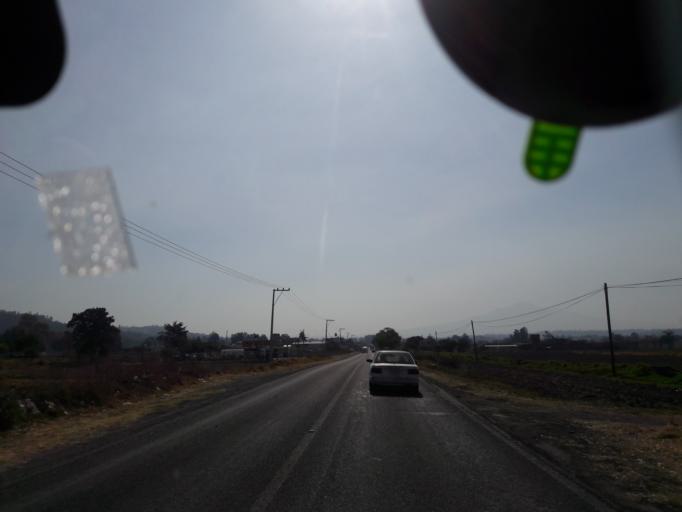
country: MX
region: Tlaxcala
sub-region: Panotla
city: Fraccionamiento la Virgen
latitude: 19.3208
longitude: -98.2919
